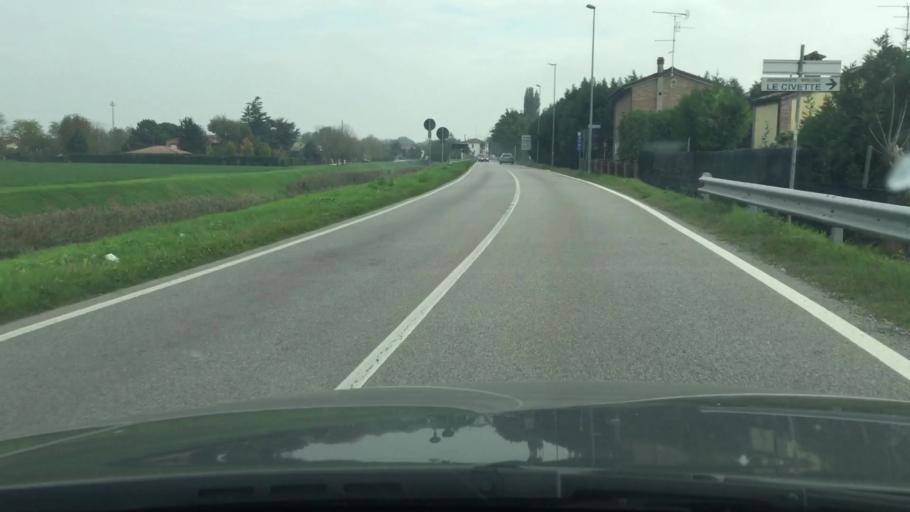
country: IT
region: Emilia-Romagna
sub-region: Provincia di Ferrara
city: Porotto-Cassama
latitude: 44.8422
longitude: 11.5755
